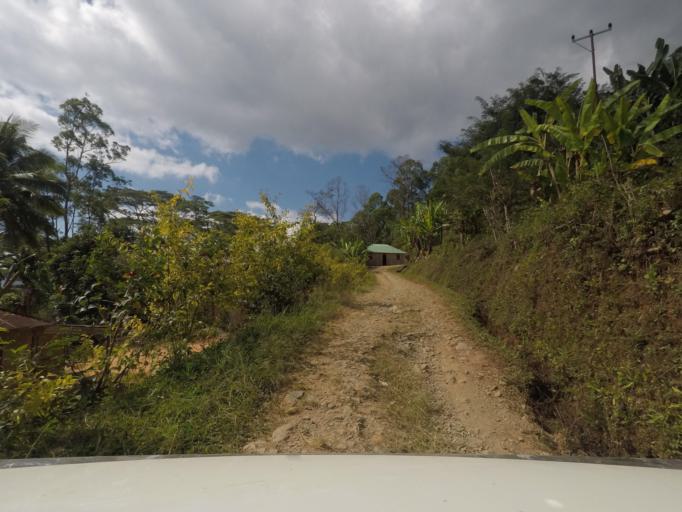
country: TL
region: Ermera
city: Gleno
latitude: -8.7192
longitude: 125.3169
